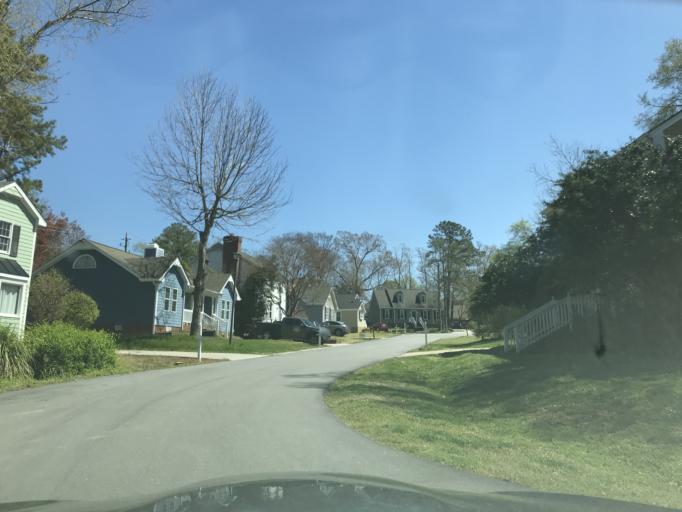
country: US
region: North Carolina
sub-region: Wake County
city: Raleigh
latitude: 35.8201
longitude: -78.5884
